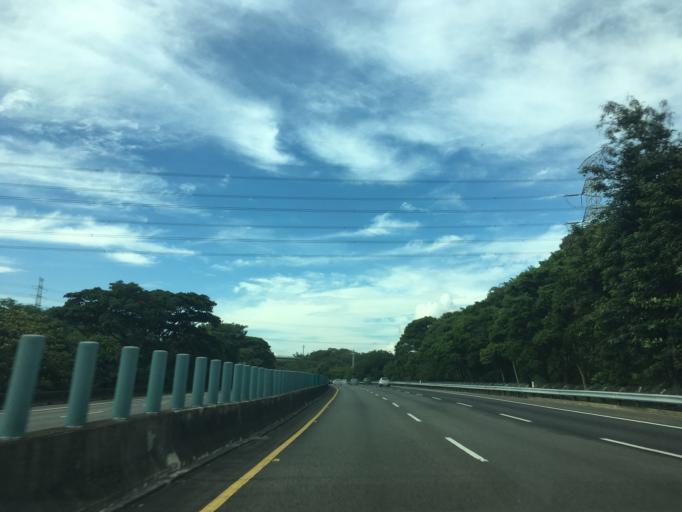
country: TW
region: Taiwan
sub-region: Chiayi
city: Jiayi Shi
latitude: 23.5441
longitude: 120.5019
